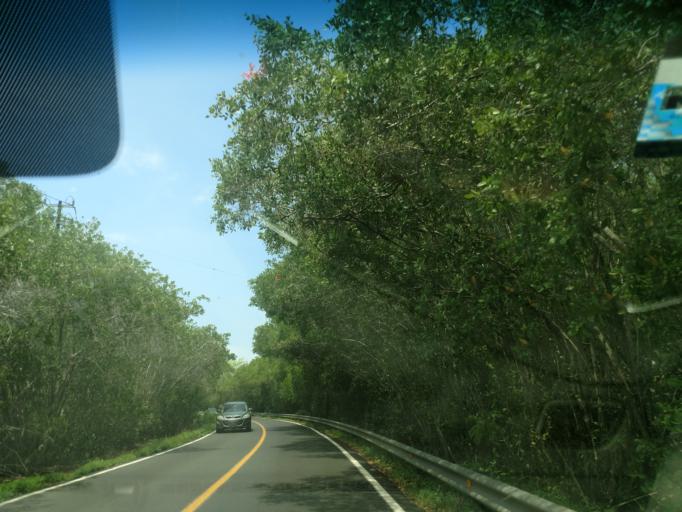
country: MX
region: Nayarit
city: San Blas
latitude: 21.5504
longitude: -105.2566
